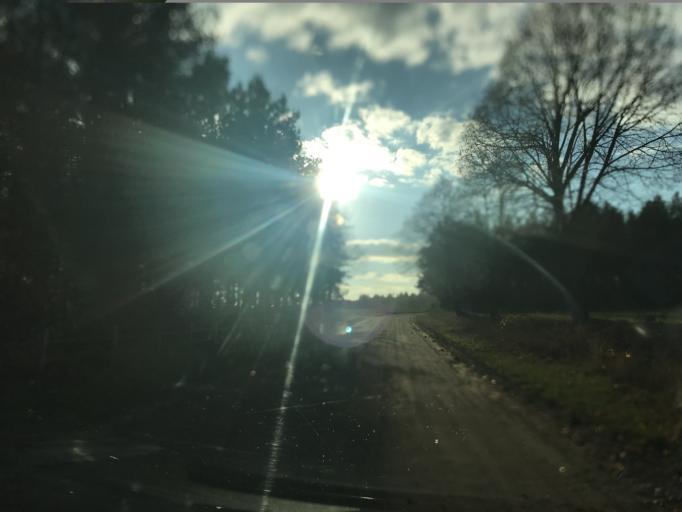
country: PL
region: Warmian-Masurian Voivodeship
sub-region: Powiat dzialdowski
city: Rybno
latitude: 53.3717
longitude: 19.8294
